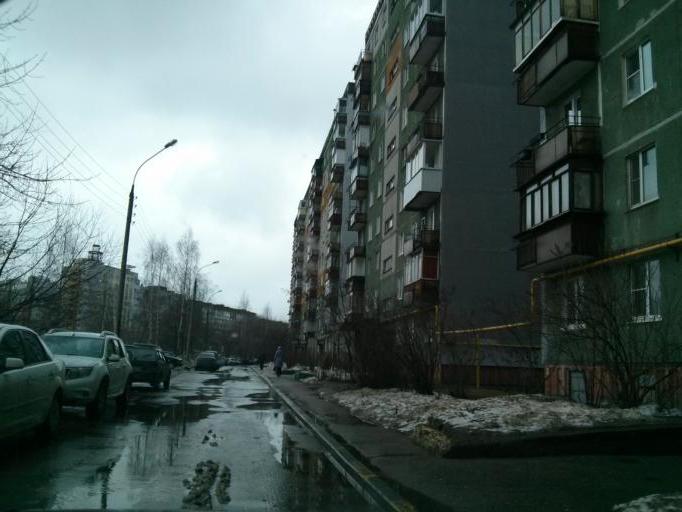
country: RU
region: Nizjnij Novgorod
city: Afonino
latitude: 56.2886
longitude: 44.0737
